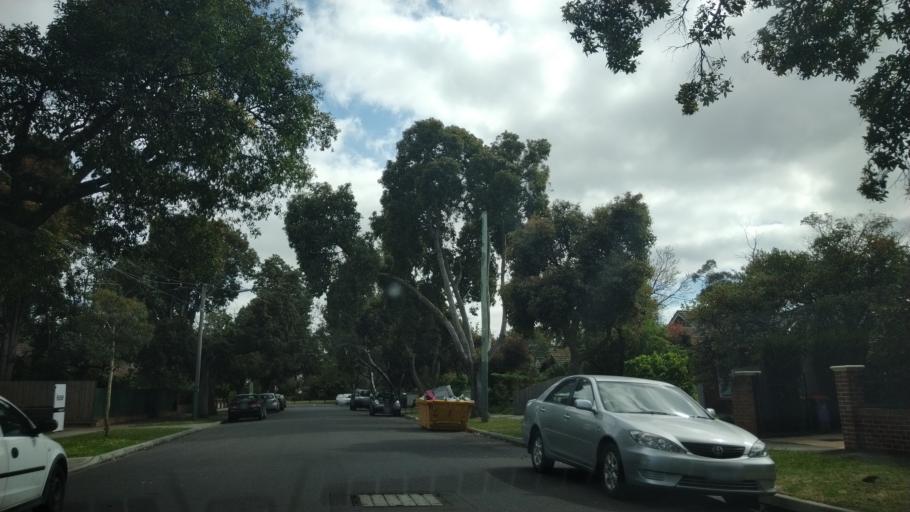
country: AU
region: Victoria
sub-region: Glen Eira
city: Glen Huntly
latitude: -37.8991
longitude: 145.0435
